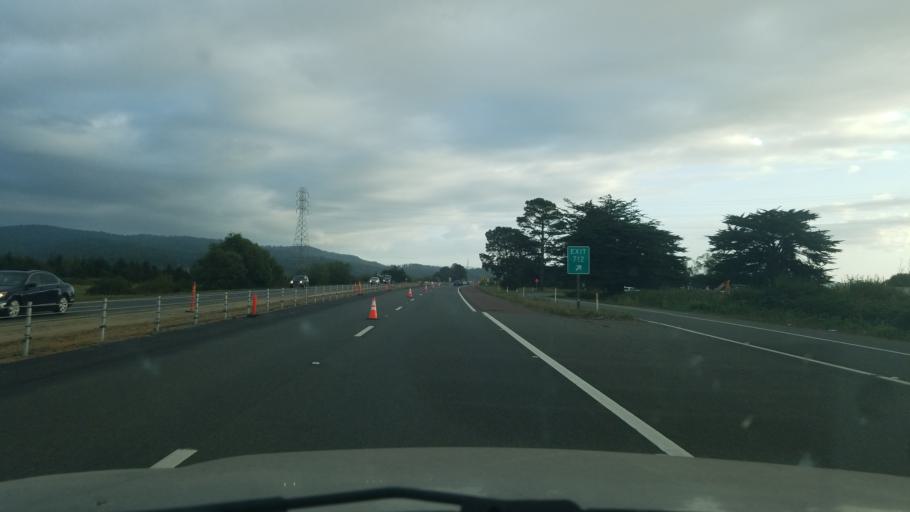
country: US
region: California
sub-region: Humboldt County
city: Arcata
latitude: 40.8529
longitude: -124.0822
